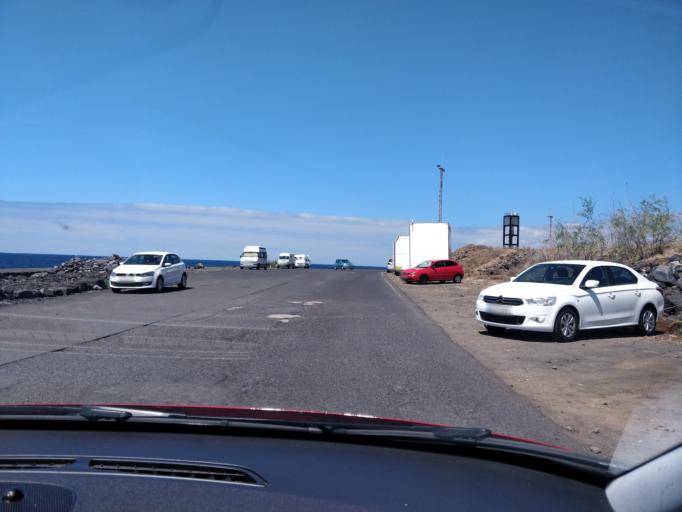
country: ES
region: Canary Islands
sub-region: Provincia de Santa Cruz de Tenerife
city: Puerto de la Cruz
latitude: 28.4174
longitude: -16.5560
